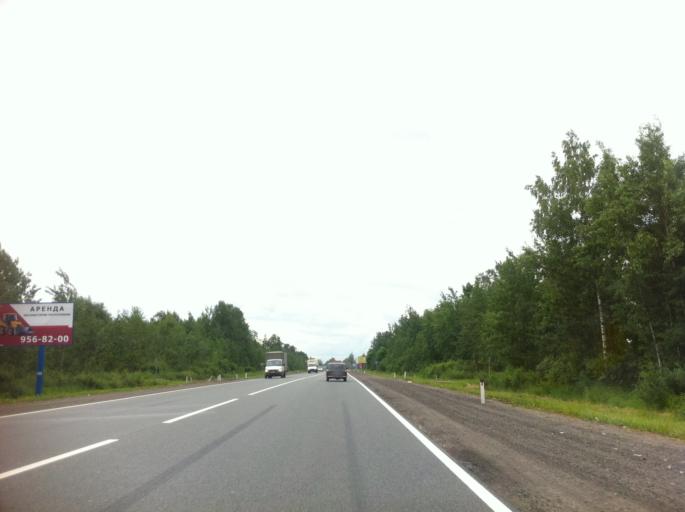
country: RU
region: Leningrad
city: Maloye Verevo
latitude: 59.6292
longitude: 30.1895
